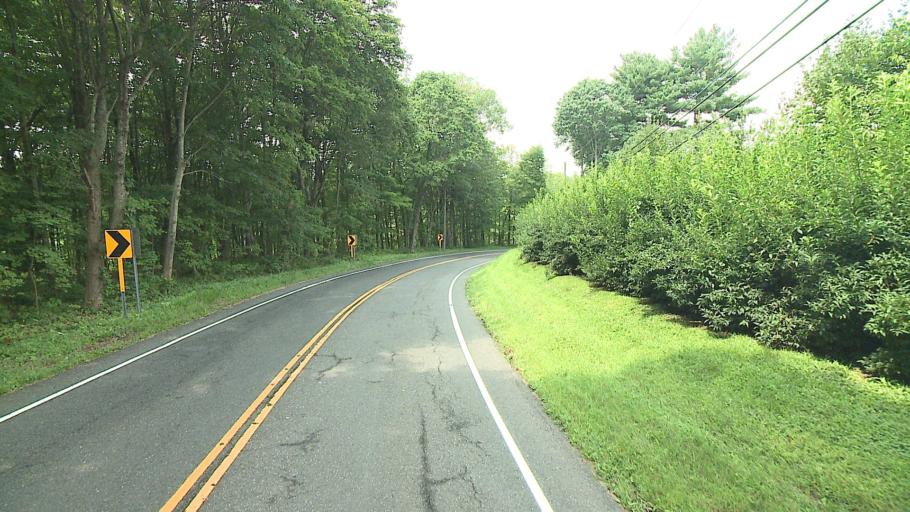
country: US
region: Connecticut
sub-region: Litchfield County
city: New Preston
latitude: 41.6346
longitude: -73.3471
